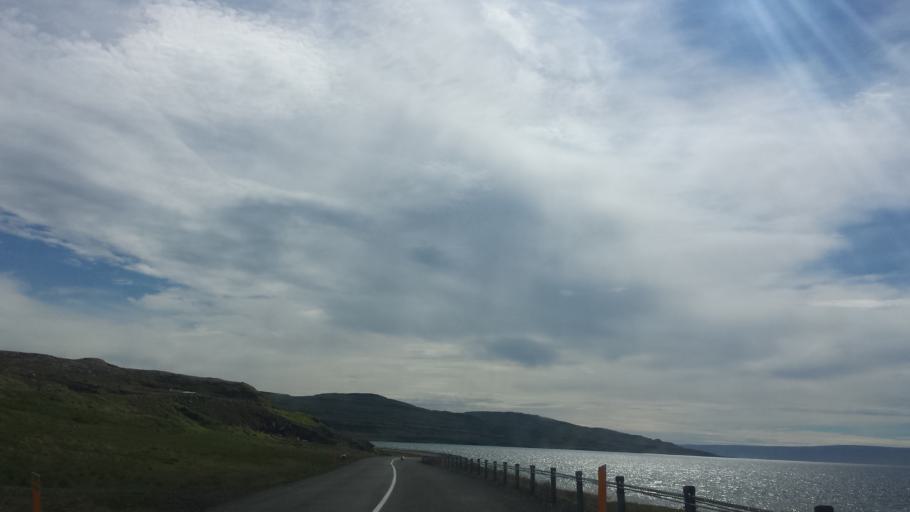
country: IS
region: West
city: Stykkisholmur
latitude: 65.7666
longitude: -21.6977
